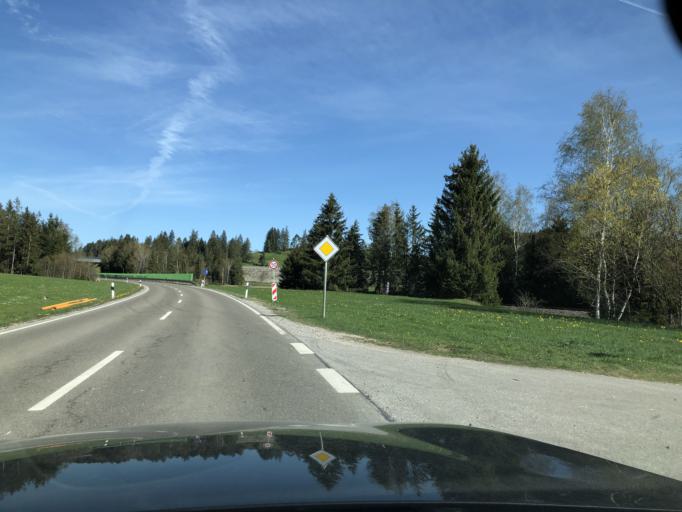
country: DE
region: Bavaria
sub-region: Swabia
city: Eisenberg
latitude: 47.6259
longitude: 10.6055
